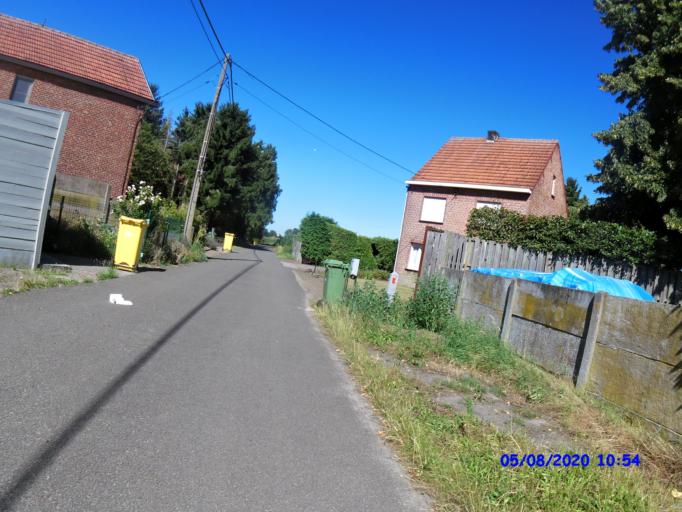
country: BE
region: Flanders
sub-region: Provincie Antwerpen
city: Vosselaar
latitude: 51.2421
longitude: 4.8908
